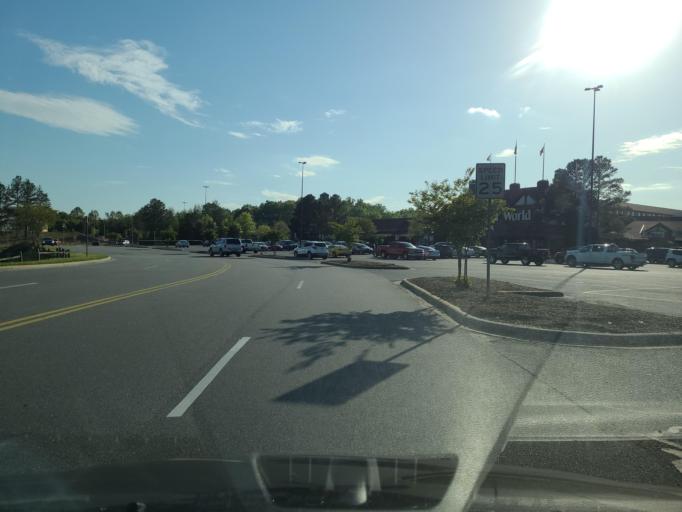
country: US
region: North Carolina
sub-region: Cabarrus County
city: Harrisburg
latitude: 35.3674
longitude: -80.7173
